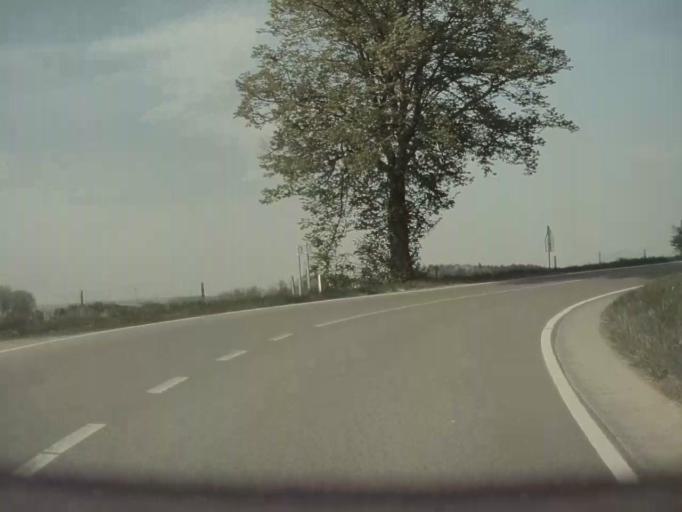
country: BE
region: Wallonia
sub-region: Province de Namur
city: Havelange
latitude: 50.3456
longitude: 5.2953
